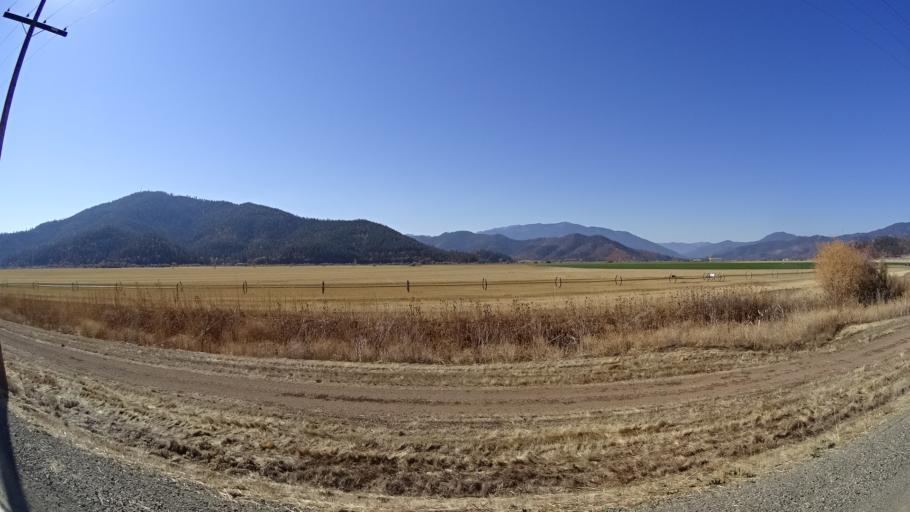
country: US
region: California
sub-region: Siskiyou County
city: Yreka
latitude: 41.6200
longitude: -122.8608
